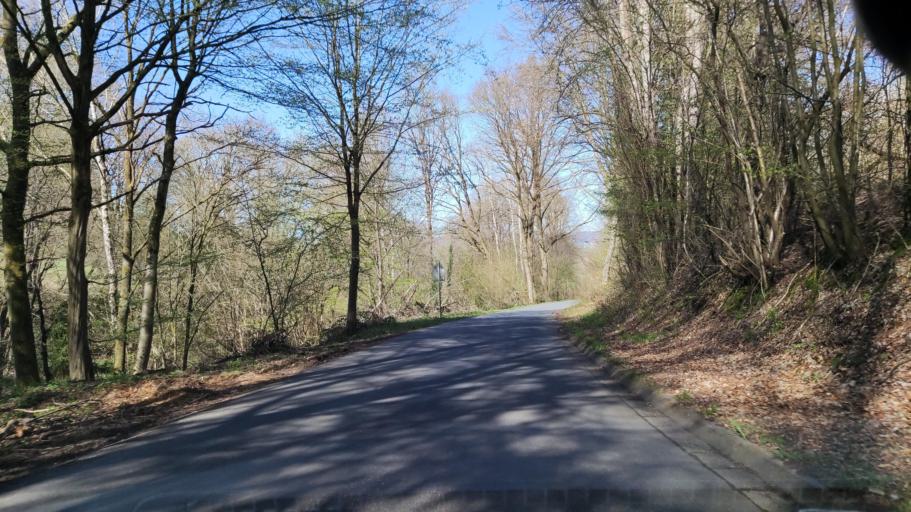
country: DE
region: Lower Saxony
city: Uslar
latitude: 51.6165
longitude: 9.6097
